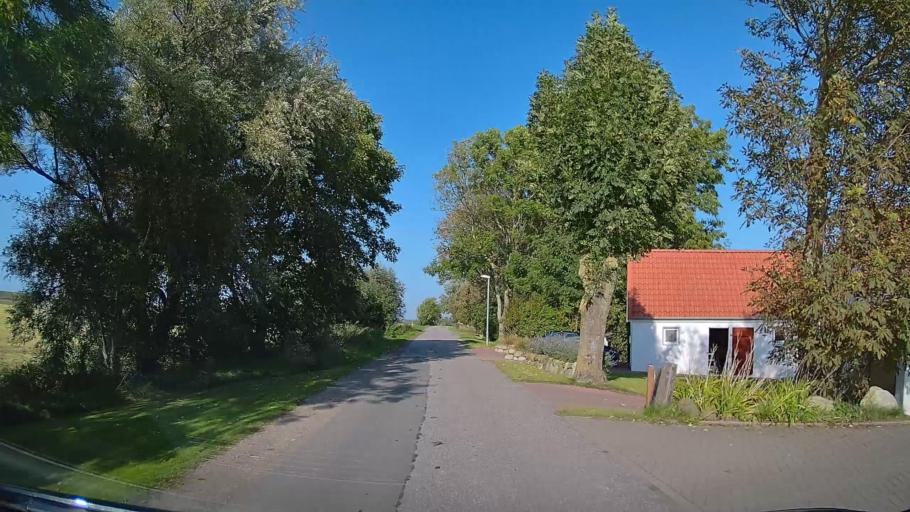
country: DE
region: Lower Saxony
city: Misselwarden
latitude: 53.6990
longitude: 8.4963
